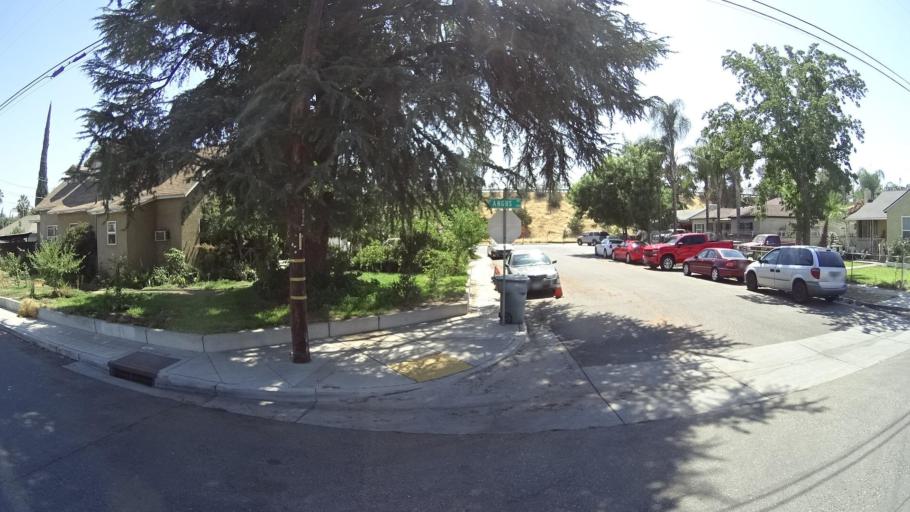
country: US
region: California
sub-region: Fresno County
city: Fresno
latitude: 36.7596
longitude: -119.7770
